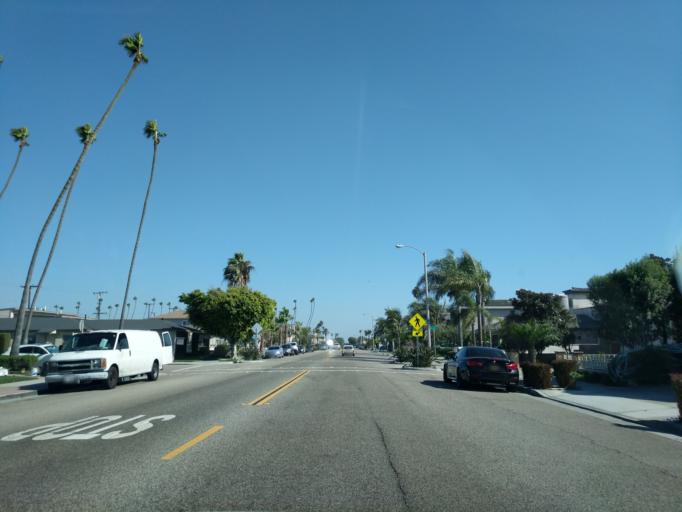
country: US
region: California
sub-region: Orange County
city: Seal Beach
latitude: 33.7413
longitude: -118.1090
